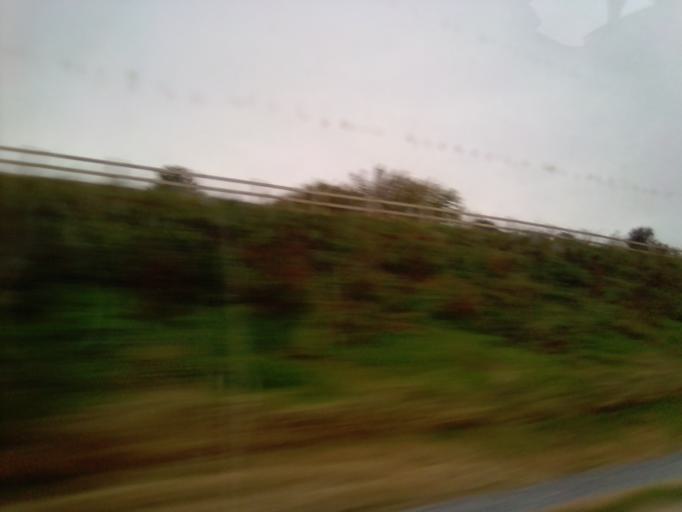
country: IE
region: Connaught
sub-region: County Galway
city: Oranmore
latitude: 53.2272
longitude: -8.8311
